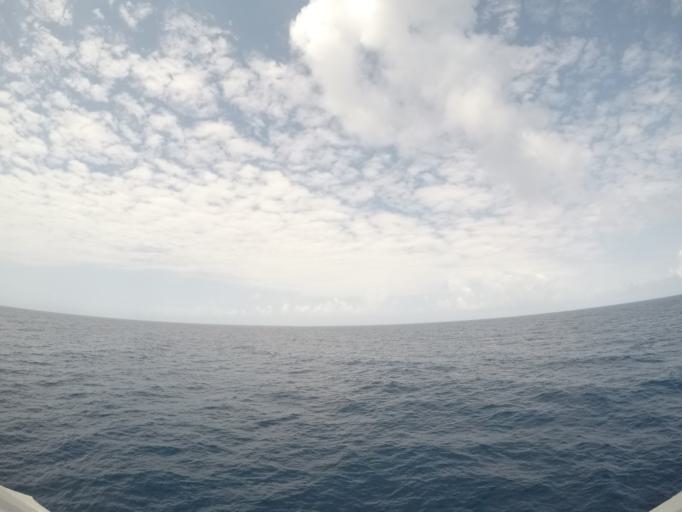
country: TZ
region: Zanzibar North
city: Nungwi
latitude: -5.5778
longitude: 39.3615
